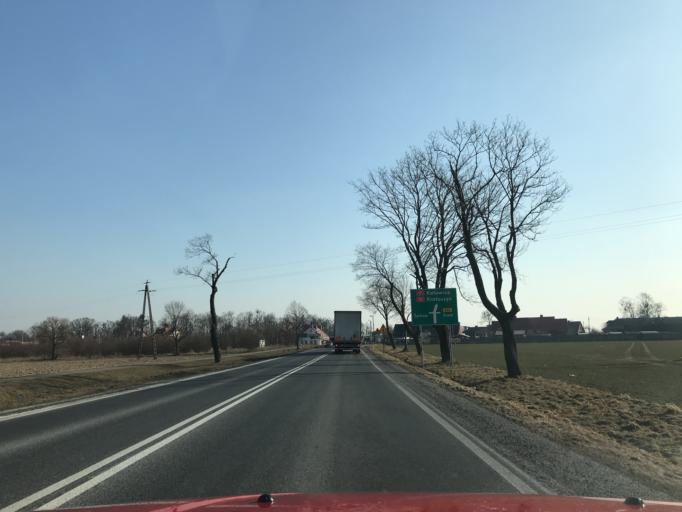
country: PL
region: Greater Poland Voivodeship
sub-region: Powiat sredzki
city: Nowe Miasto nad Warta
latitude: 52.0776
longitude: 17.4176
